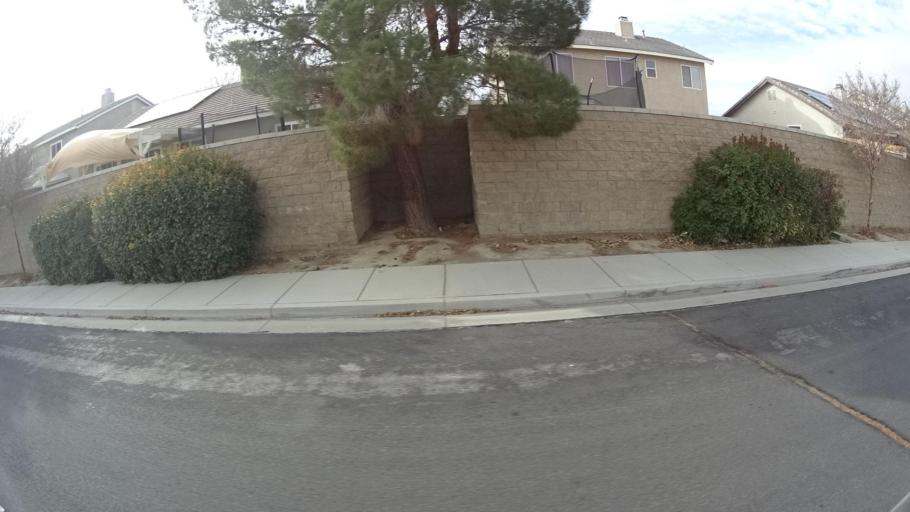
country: US
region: California
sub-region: Kern County
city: Rosamond
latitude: 34.8520
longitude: -118.1937
